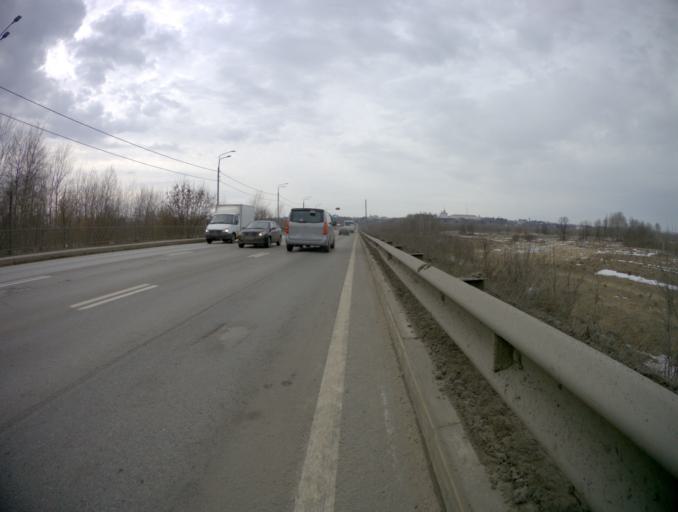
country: RU
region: Vladimir
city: Kommunar
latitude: 56.1145
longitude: 40.4224
